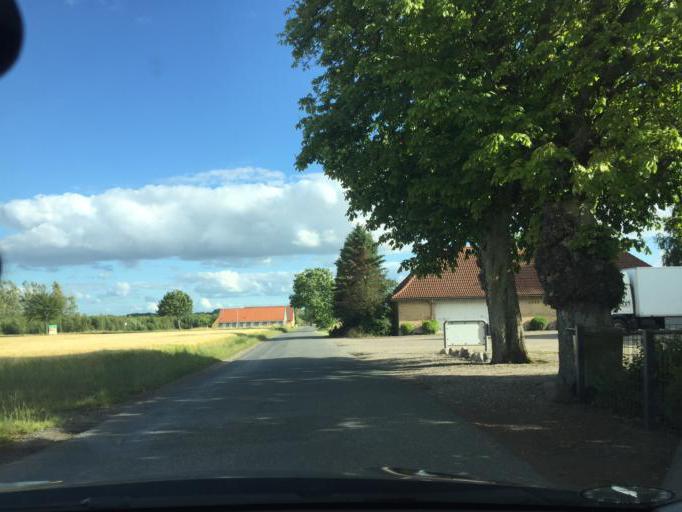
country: DK
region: South Denmark
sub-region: Faaborg-Midtfyn Kommune
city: Arslev
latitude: 55.2893
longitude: 10.5401
